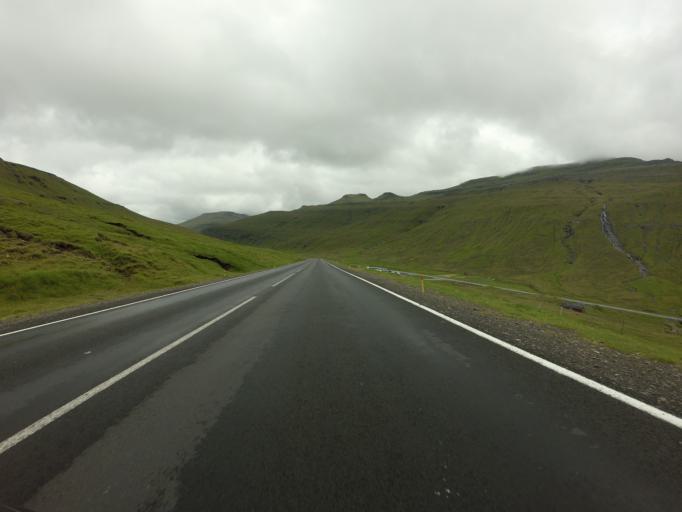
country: FO
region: Streymoy
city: Kollafjordhur
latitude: 62.1152
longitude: -6.9832
